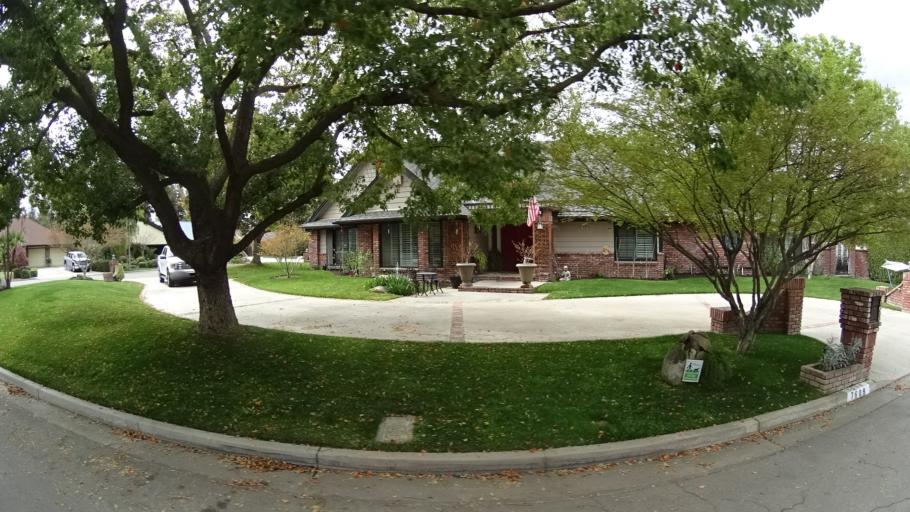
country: US
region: California
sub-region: Fresno County
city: Fresno
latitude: 36.8482
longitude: -119.8435
